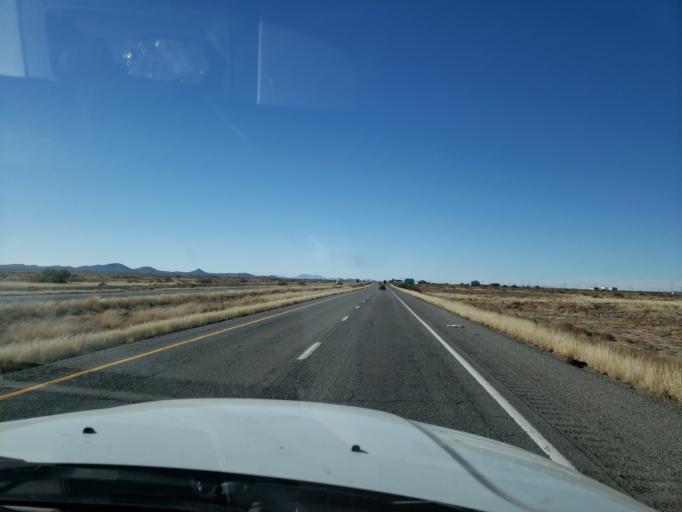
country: US
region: New Mexico
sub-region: Hidalgo County
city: Lordsburg
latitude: 32.3318
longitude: -108.6469
